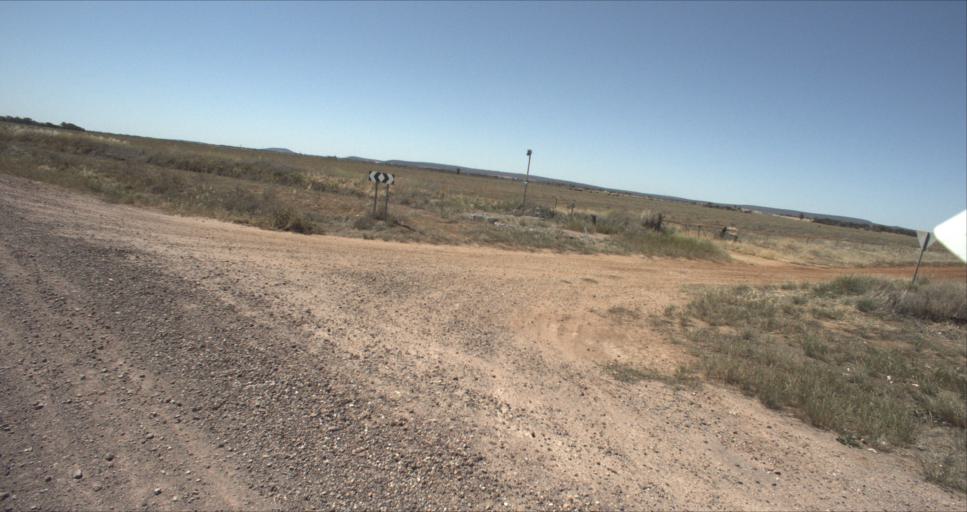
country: AU
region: New South Wales
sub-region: Leeton
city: Leeton
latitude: -34.5014
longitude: 146.3440
